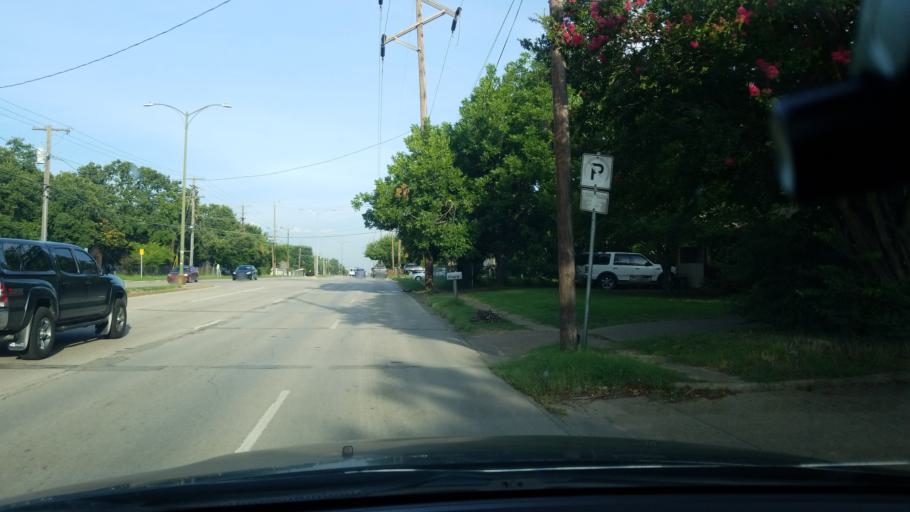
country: US
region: Texas
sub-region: Dallas County
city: Balch Springs
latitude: 32.7196
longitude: -96.6577
